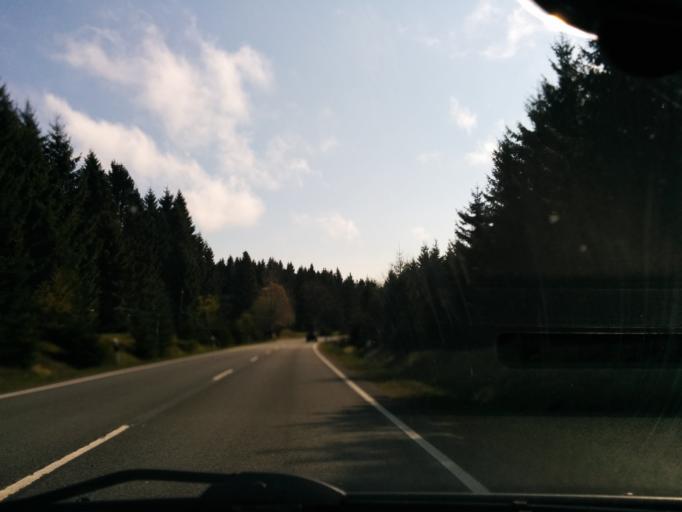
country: DE
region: Lower Saxony
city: Altenau
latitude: 51.7904
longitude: 10.3923
